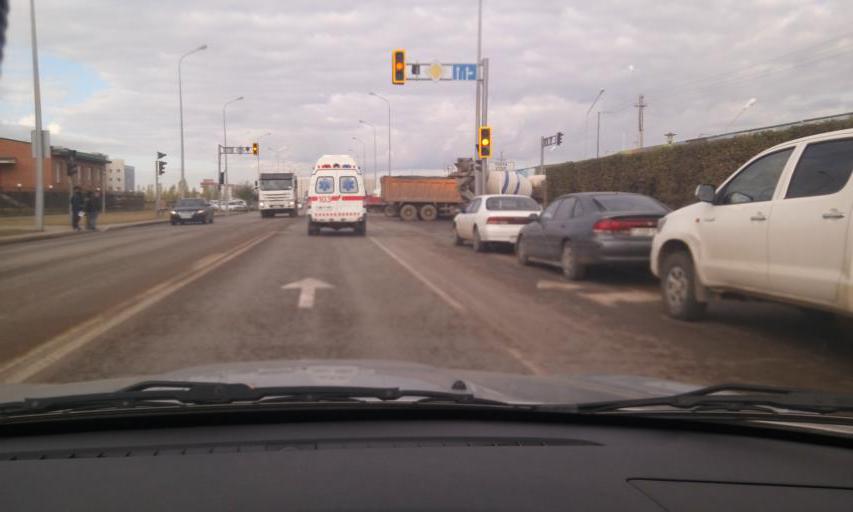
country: KZ
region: Astana Qalasy
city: Astana
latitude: 51.0848
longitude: 71.4136
